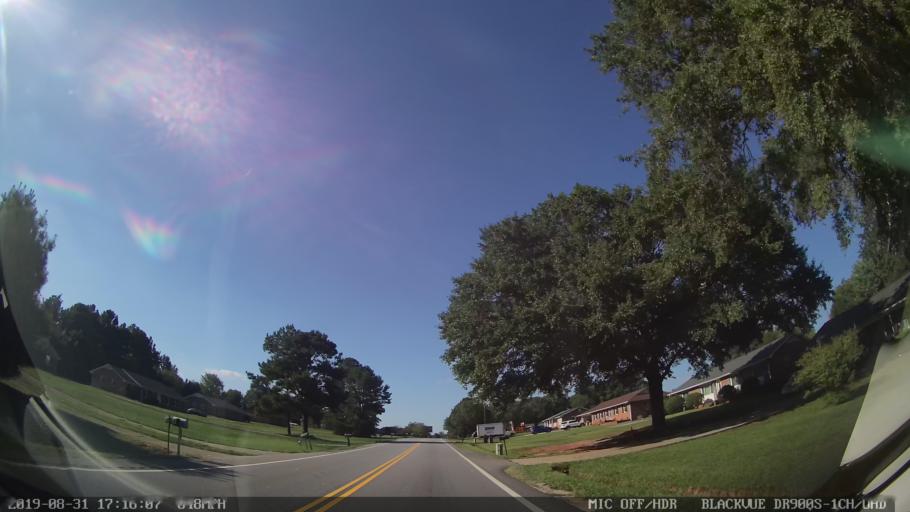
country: US
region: South Carolina
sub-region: Spartanburg County
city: Valley Falls
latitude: 35.0202
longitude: -81.9496
